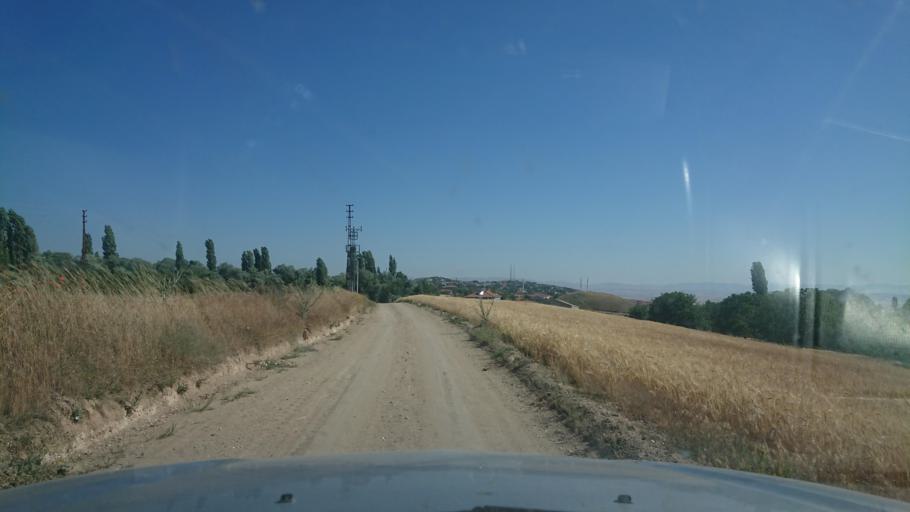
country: TR
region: Aksaray
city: Agacoren
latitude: 38.8599
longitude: 33.9121
